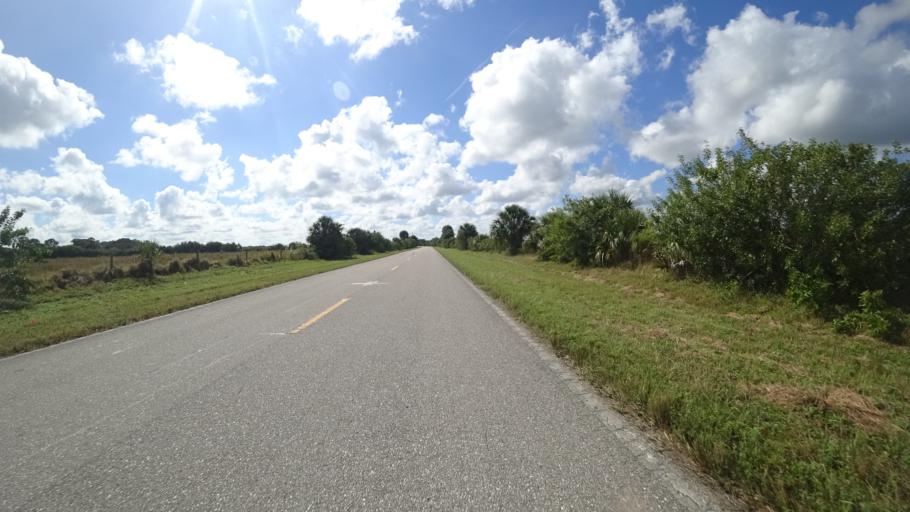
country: US
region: Florida
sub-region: Manatee County
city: Ellenton
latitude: 27.6139
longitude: -82.4819
